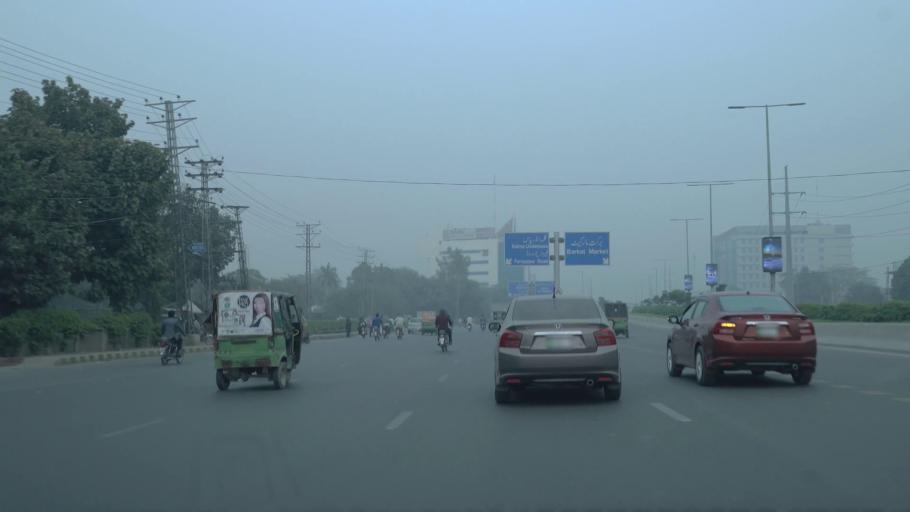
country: PK
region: Punjab
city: Lahore
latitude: 31.5026
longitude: 74.3254
